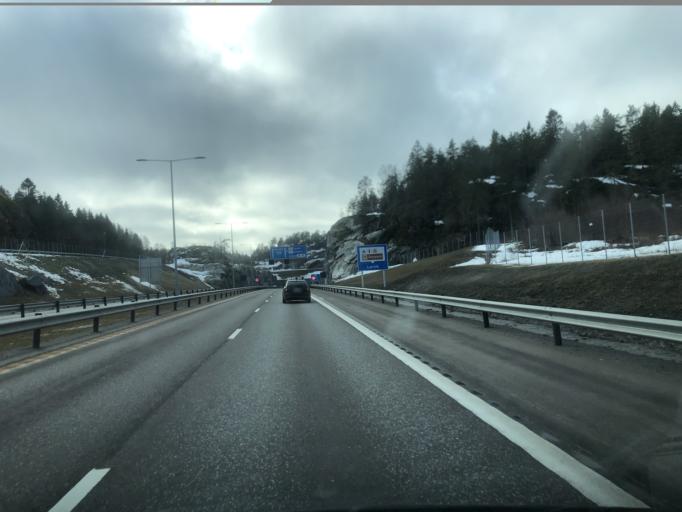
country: NO
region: Vestfold
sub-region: Larvik
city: Larvik
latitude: 59.0832
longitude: 10.0566
